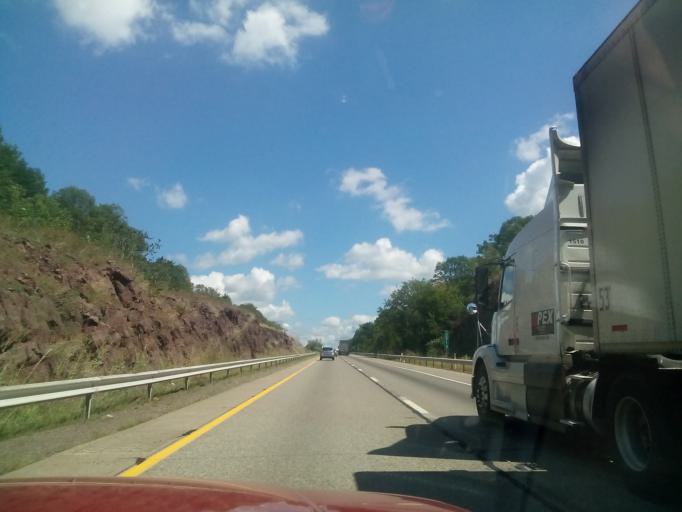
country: US
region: Pennsylvania
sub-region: Luzerne County
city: Nescopeck
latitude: 41.0041
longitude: -76.1530
